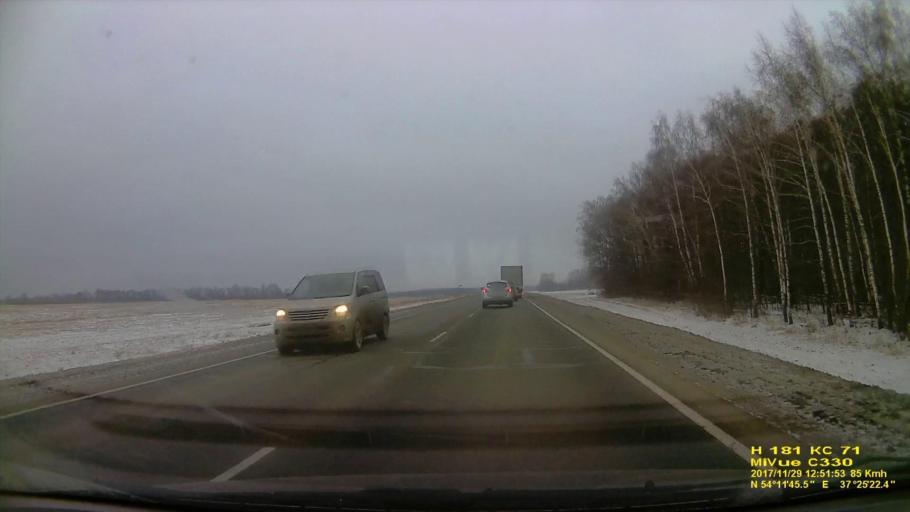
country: RU
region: Tula
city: Barsuki
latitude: 54.1961
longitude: 37.4227
